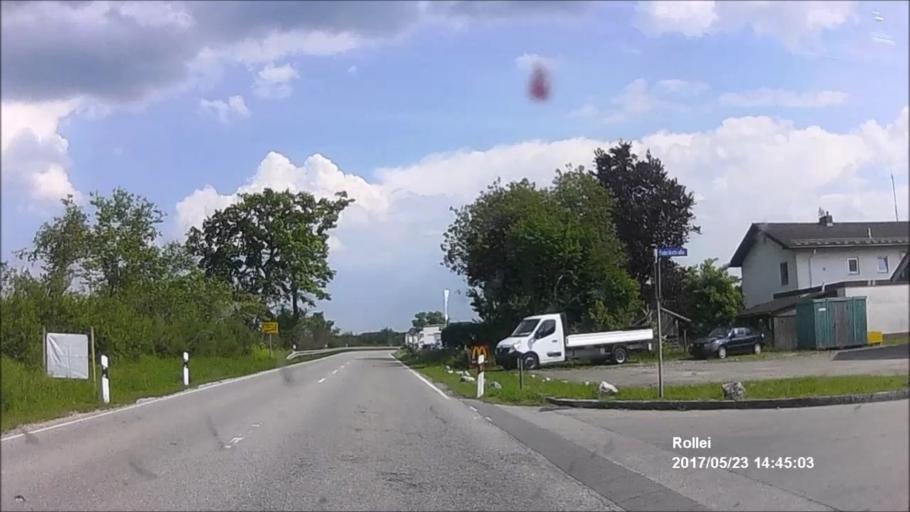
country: DE
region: Bavaria
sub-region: Upper Bavaria
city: Trostberg an der Alz
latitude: 47.9847
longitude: 12.5497
